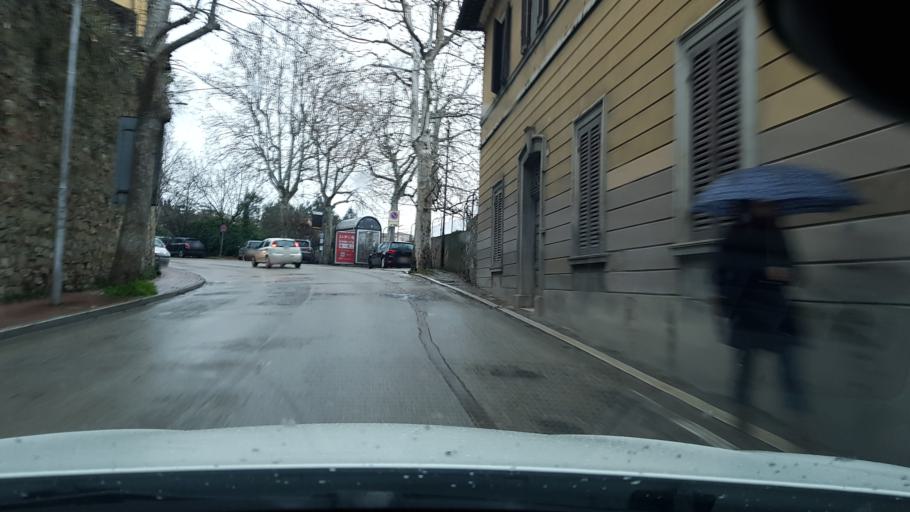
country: IT
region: Umbria
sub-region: Provincia di Perugia
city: Perugia
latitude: 43.1119
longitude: 12.3940
